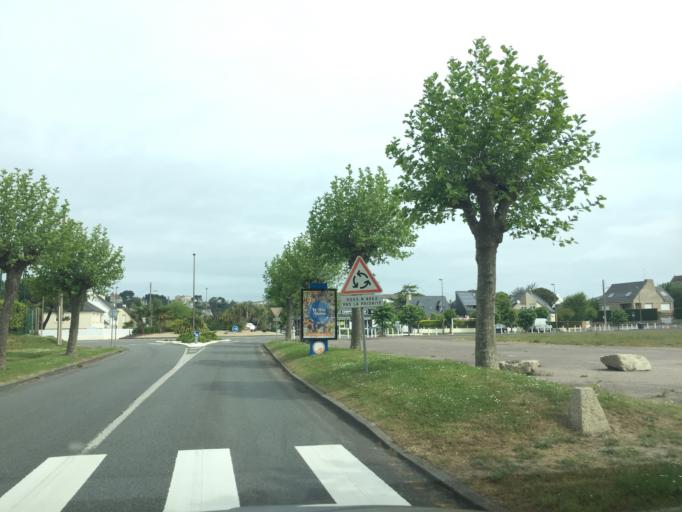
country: FR
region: Brittany
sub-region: Departement des Cotes-d'Armor
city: Saint-Cast-le-Guildo
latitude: 48.6281
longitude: -2.2545
